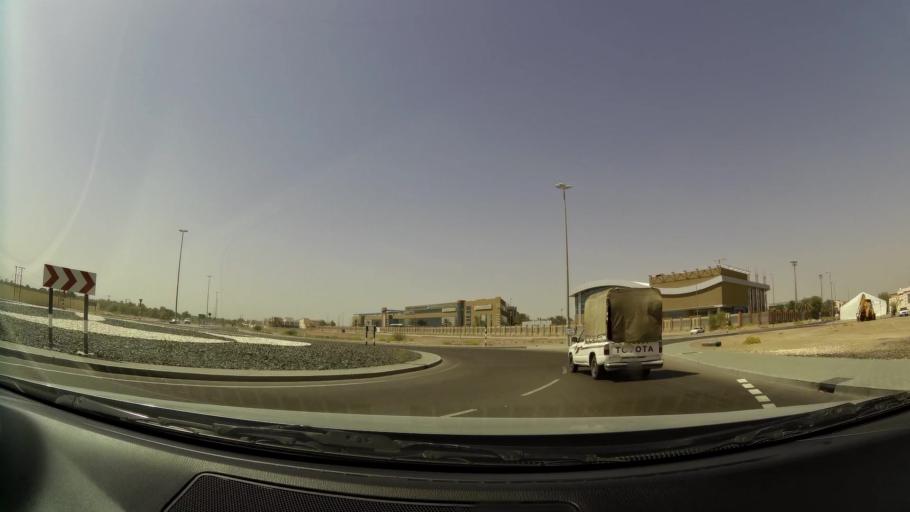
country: OM
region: Al Buraimi
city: Al Buraymi
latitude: 24.3064
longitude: 55.7615
